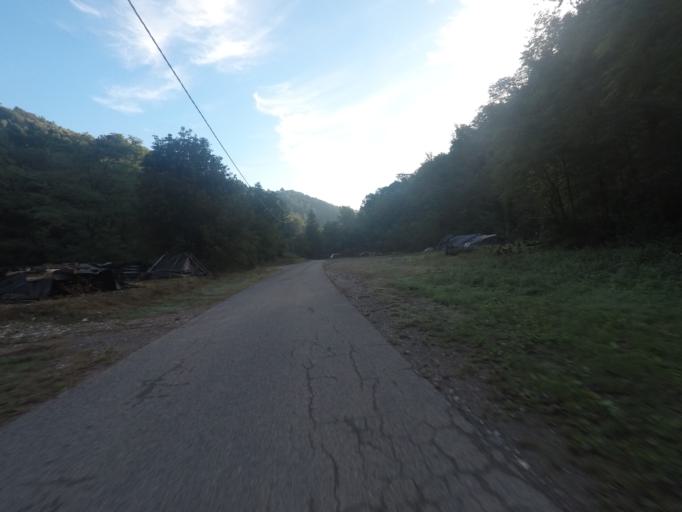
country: IT
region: Tuscany
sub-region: Provincia di Lucca
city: Pescaglia
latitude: 43.9502
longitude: 10.4166
